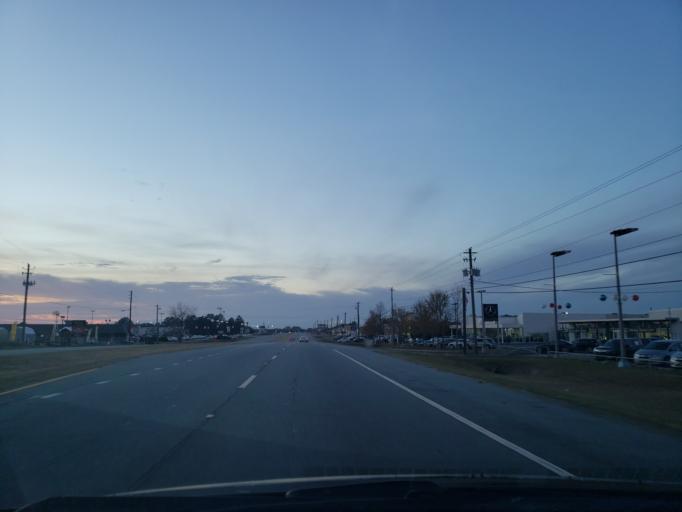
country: US
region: Georgia
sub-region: Dougherty County
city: Albany
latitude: 31.5730
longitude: -84.1306
